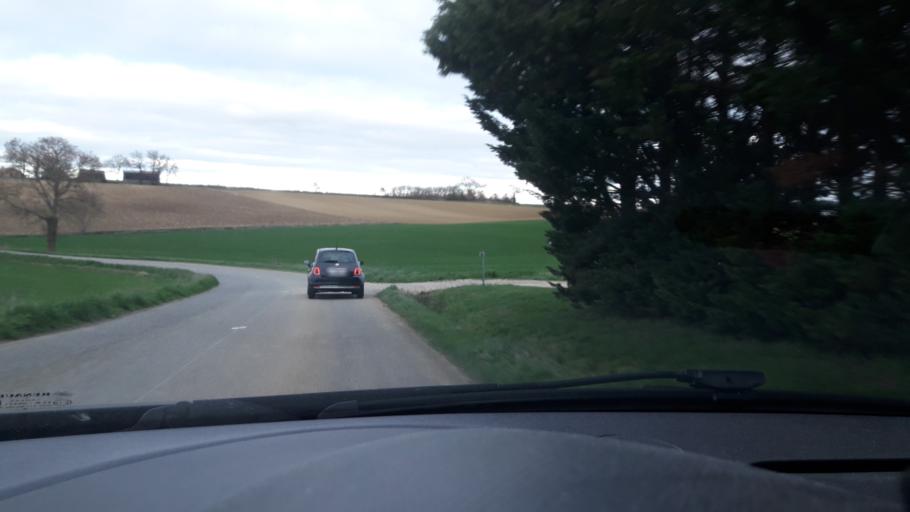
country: FR
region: Midi-Pyrenees
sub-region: Departement du Gers
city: Pujaudran
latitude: 43.6766
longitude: 1.0383
